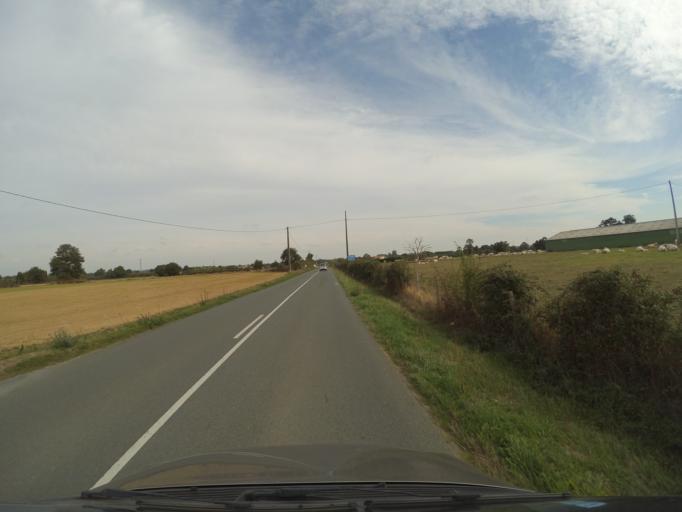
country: FR
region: Pays de la Loire
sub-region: Departement de Maine-et-Loire
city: Melay
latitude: 47.2136
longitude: -0.6230
